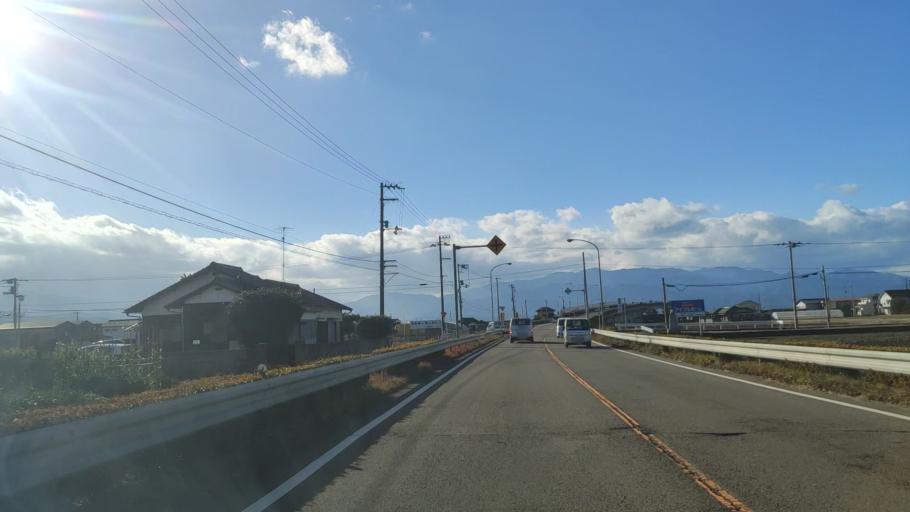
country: JP
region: Ehime
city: Saijo
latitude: 33.9156
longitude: 133.1388
